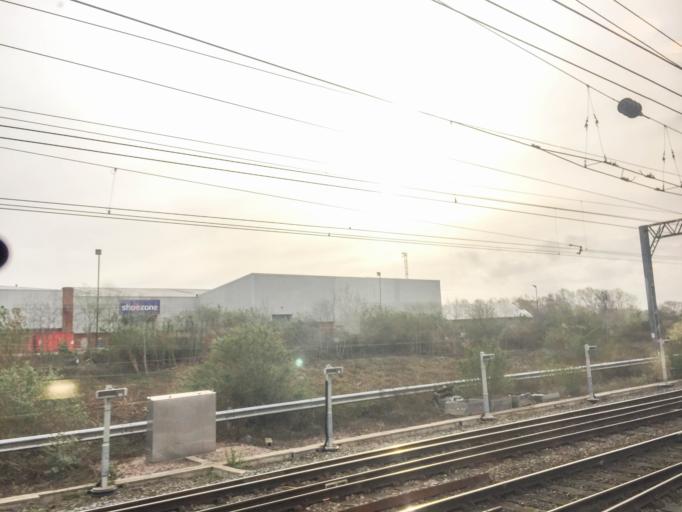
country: GB
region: England
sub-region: Cheshire East
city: Crewe
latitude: 53.0953
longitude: -2.4359
